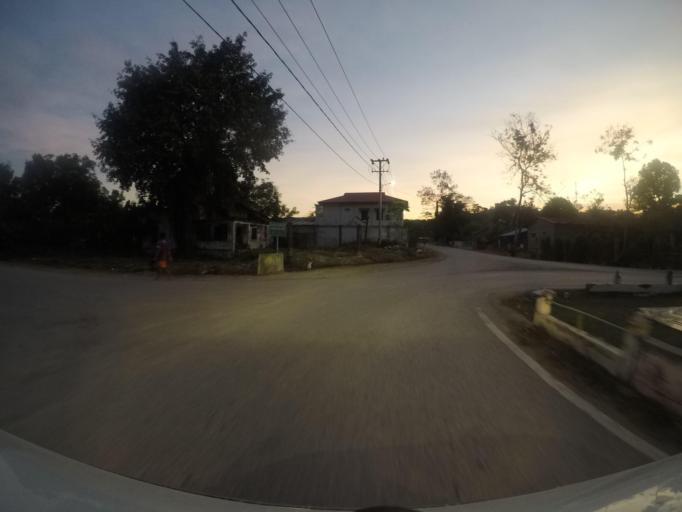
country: TL
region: Viqueque
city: Viqueque
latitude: -8.8695
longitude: 126.3668
